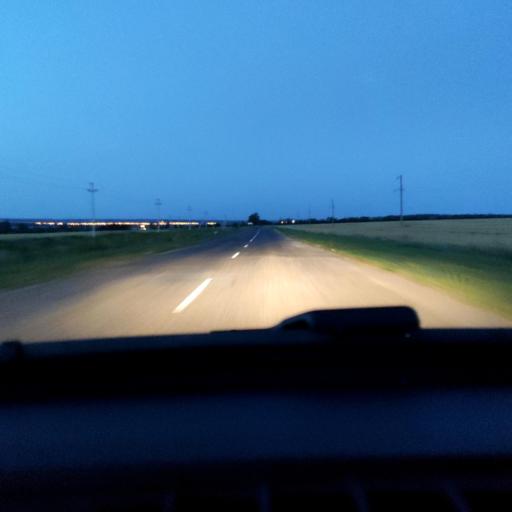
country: RU
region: Lipetsk
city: Zadonsk
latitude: 52.3110
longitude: 38.9063
